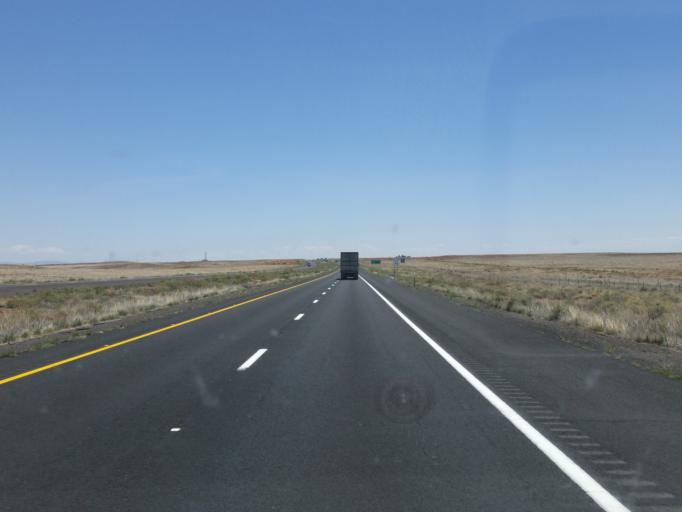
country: US
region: Arizona
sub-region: Coconino County
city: LeChee
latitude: 35.1155
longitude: -111.0788
